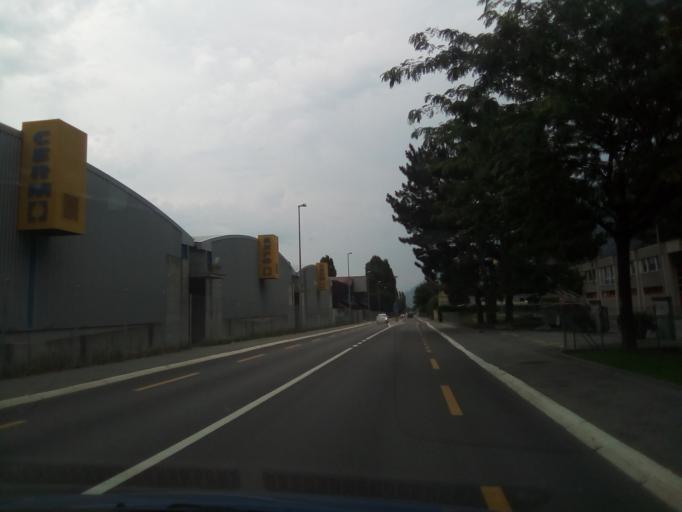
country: CH
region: Valais
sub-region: Martigny District
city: Martigny-Ville
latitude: 46.0971
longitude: 7.0777
